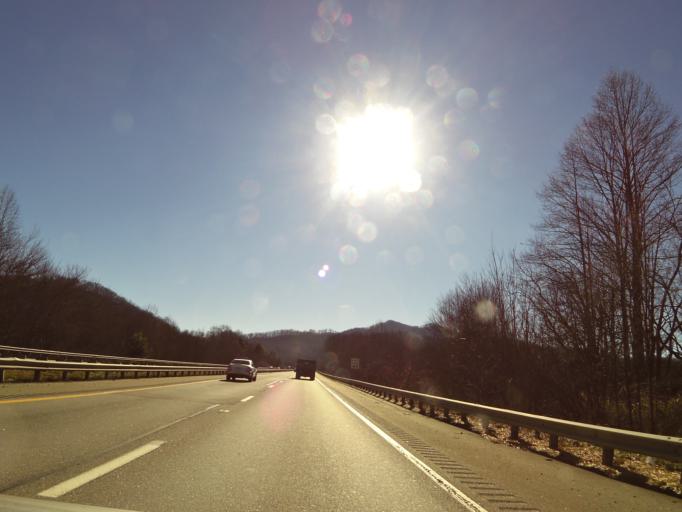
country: US
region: North Carolina
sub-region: Haywood County
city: Cove Creek
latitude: 35.5931
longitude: -82.9999
